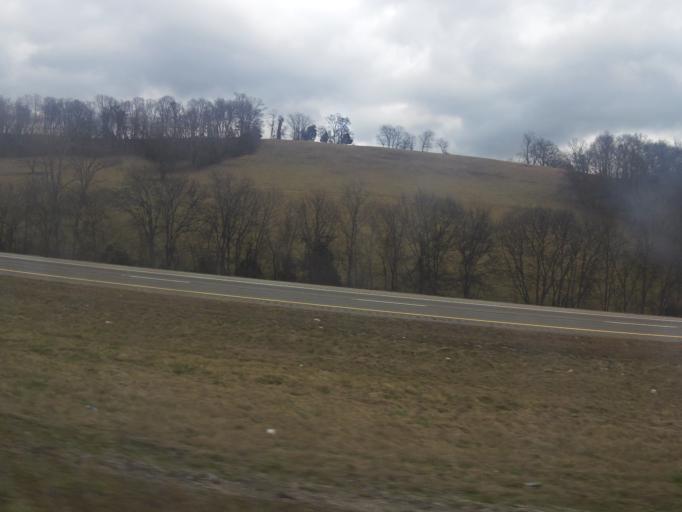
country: US
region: Tennessee
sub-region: Rutherford County
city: Plainview
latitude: 35.5892
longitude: -86.2378
